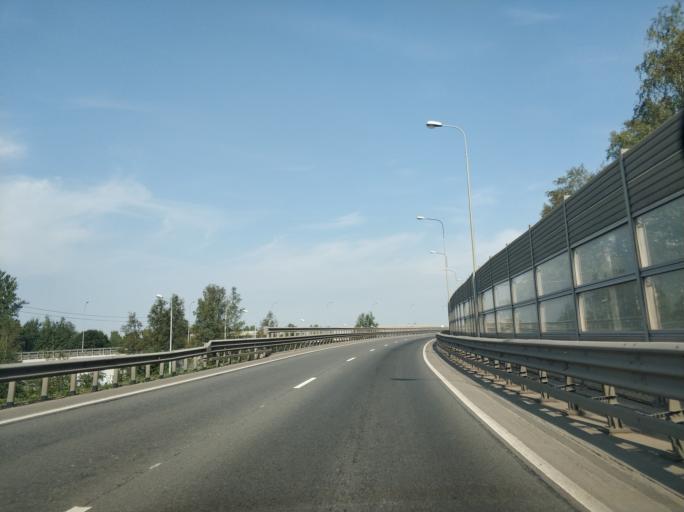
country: RU
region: St.-Petersburg
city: Krasnogvargeisky
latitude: 59.9791
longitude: 30.5060
